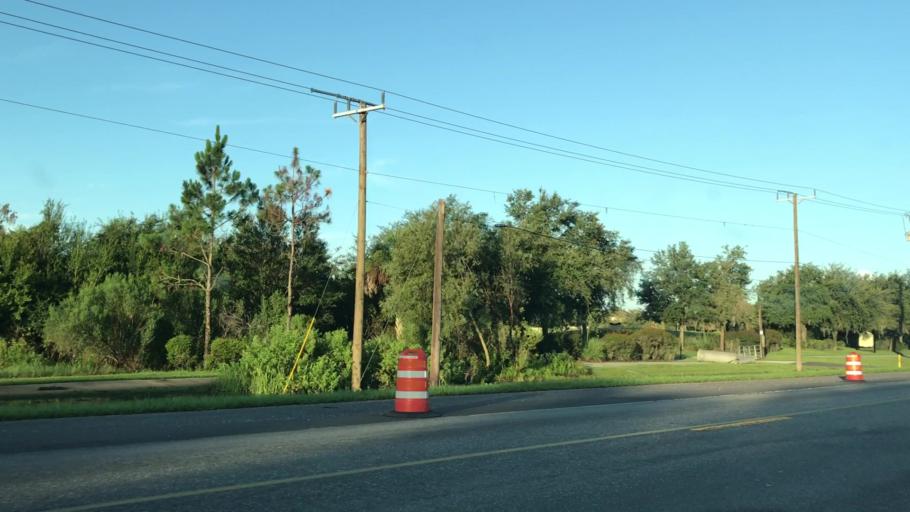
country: US
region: Florida
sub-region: Sarasota County
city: Lake Sarasota
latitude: 27.3387
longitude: -82.3837
